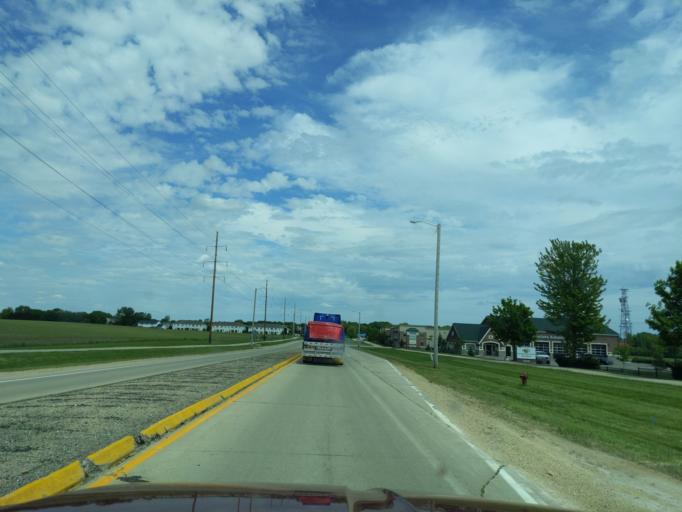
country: US
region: Wisconsin
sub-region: Dane County
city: Sun Prairie
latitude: 43.1869
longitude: -89.2623
